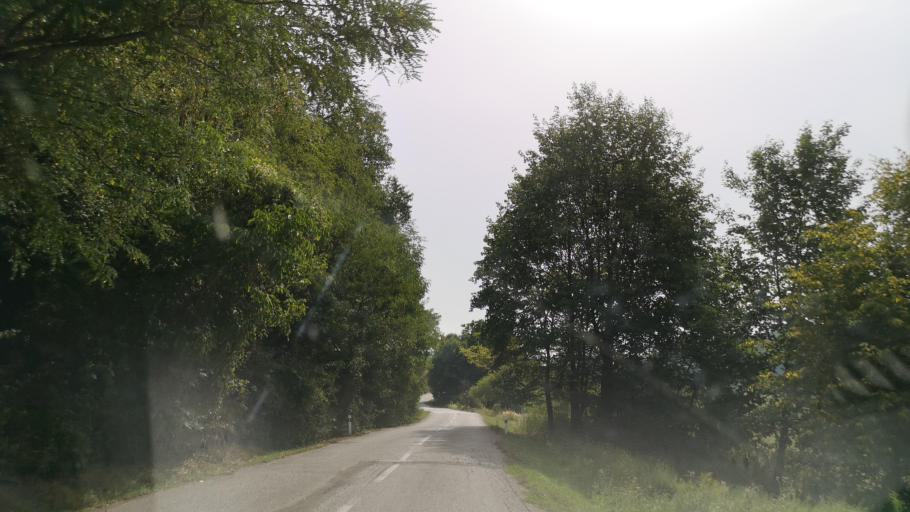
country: SK
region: Banskobystricky
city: Revuca
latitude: 48.6022
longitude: 20.1308
